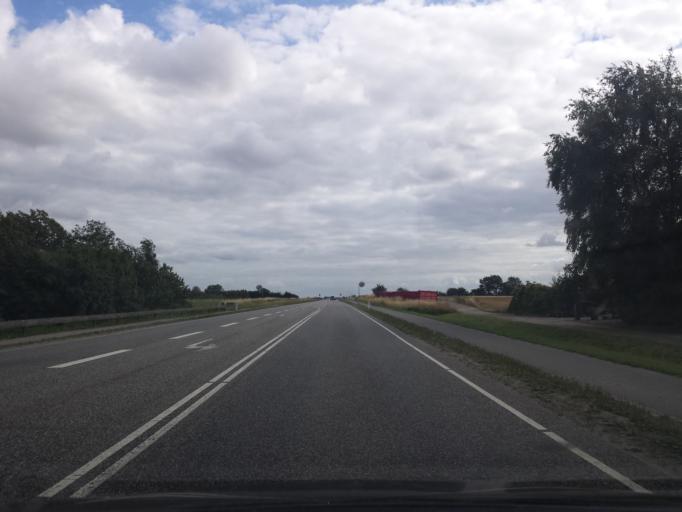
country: DK
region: South Denmark
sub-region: Sonderborg Kommune
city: Augustenborg
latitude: 54.9637
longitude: 9.8994
